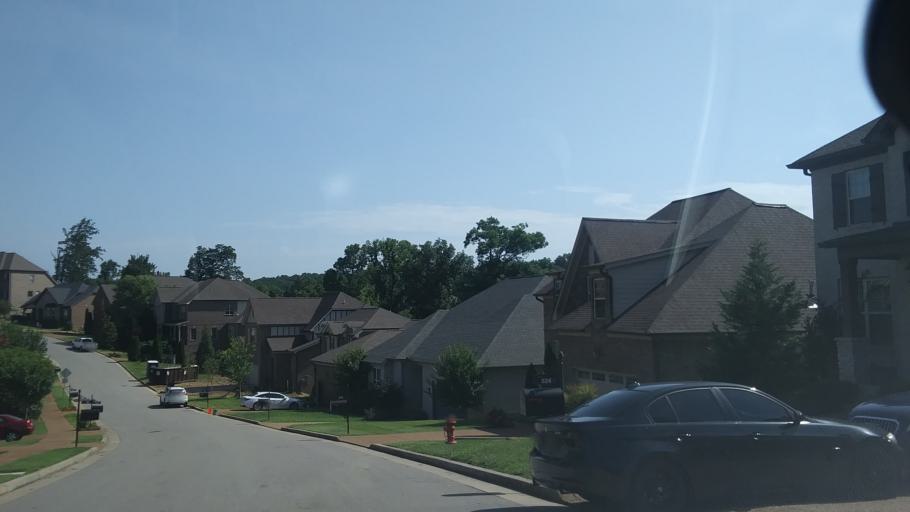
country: US
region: Tennessee
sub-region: Davidson County
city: Belle Meade
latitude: 36.0843
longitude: -86.9221
